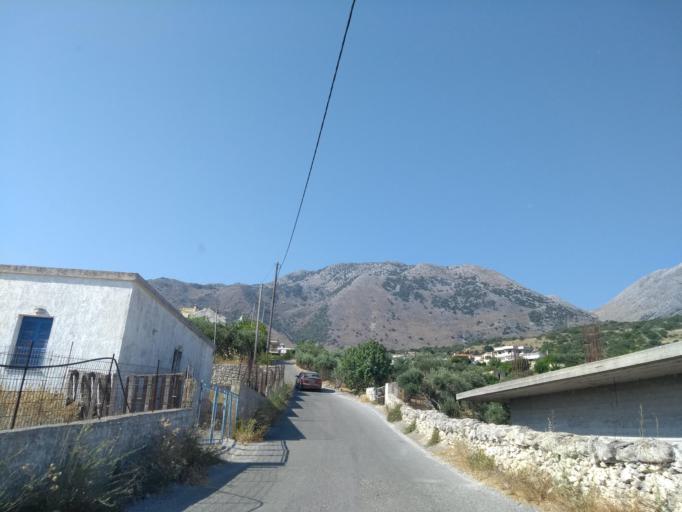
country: GR
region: Crete
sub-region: Nomos Chanias
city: Georgioupolis
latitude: 35.3171
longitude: 24.2960
